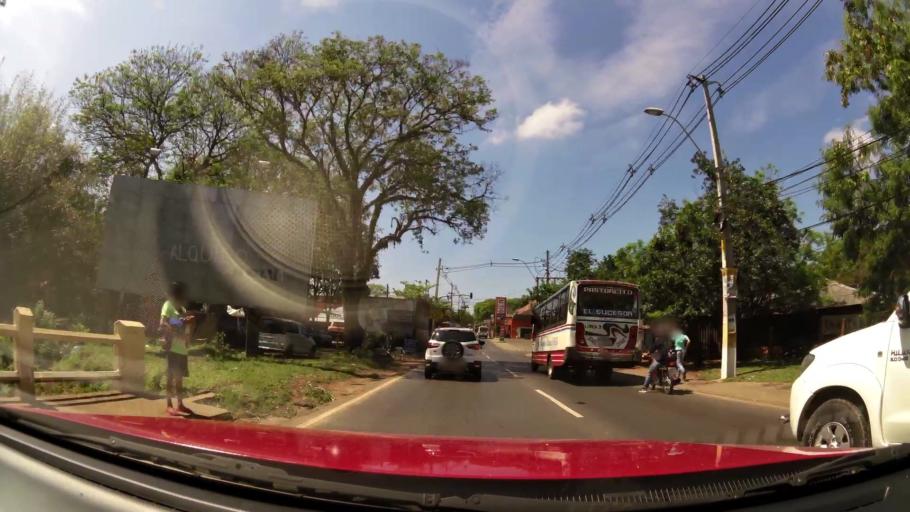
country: PY
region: Central
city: San Lorenzo
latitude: -25.3383
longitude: -57.5098
